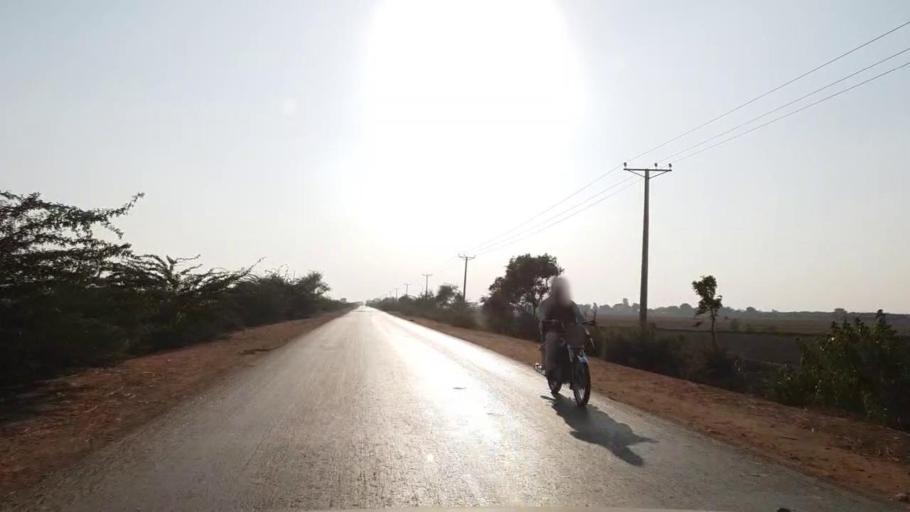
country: PK
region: Sindh
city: Bulri
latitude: 24.7970
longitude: 68.3037
